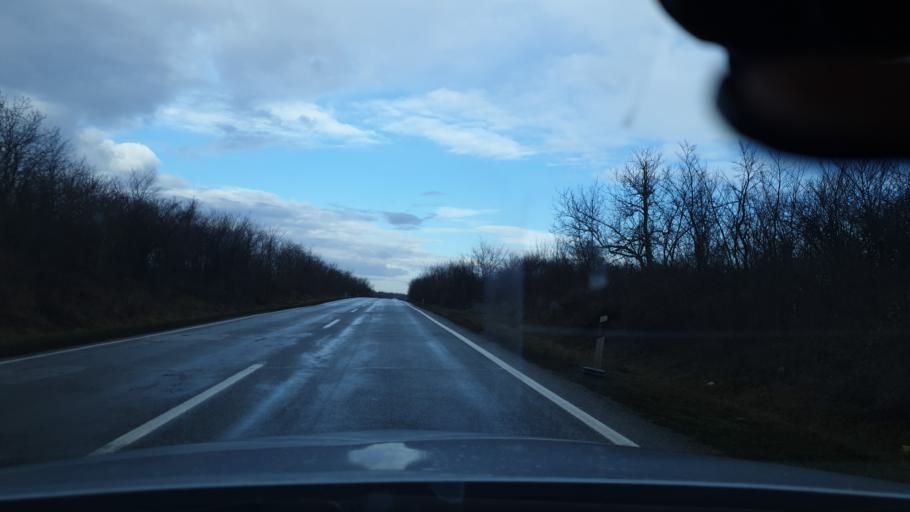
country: RS
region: Central Serbia
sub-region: Podunavski Okrug
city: Smederevo
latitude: 44.5994
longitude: 20.9557
